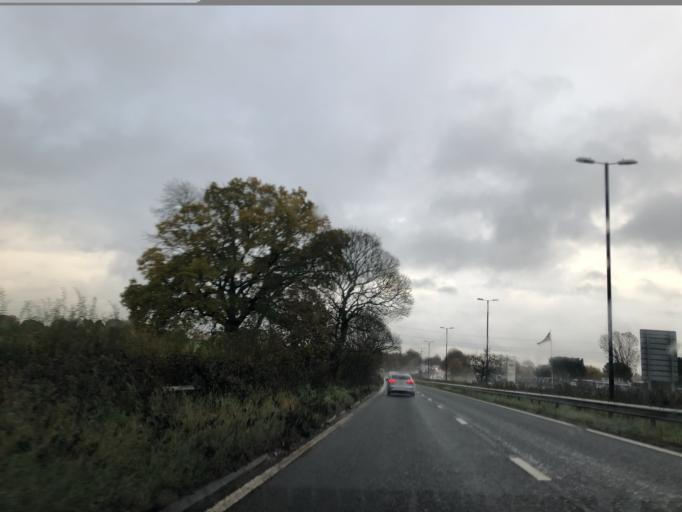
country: GB
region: England
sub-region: Solihull
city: Meriden
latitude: 52.4328
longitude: -1.5962
